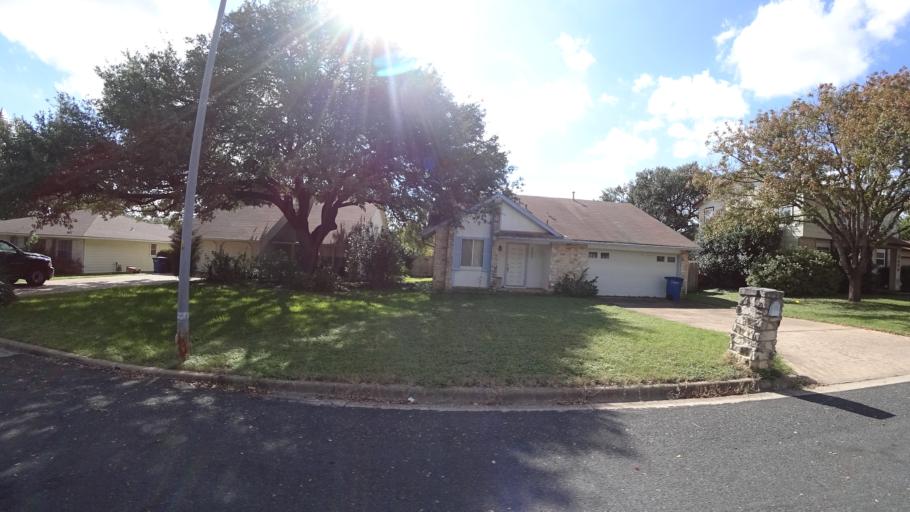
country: US
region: Texas
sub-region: Travis County
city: Wells Branch
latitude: 30.4171
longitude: -97.7199
